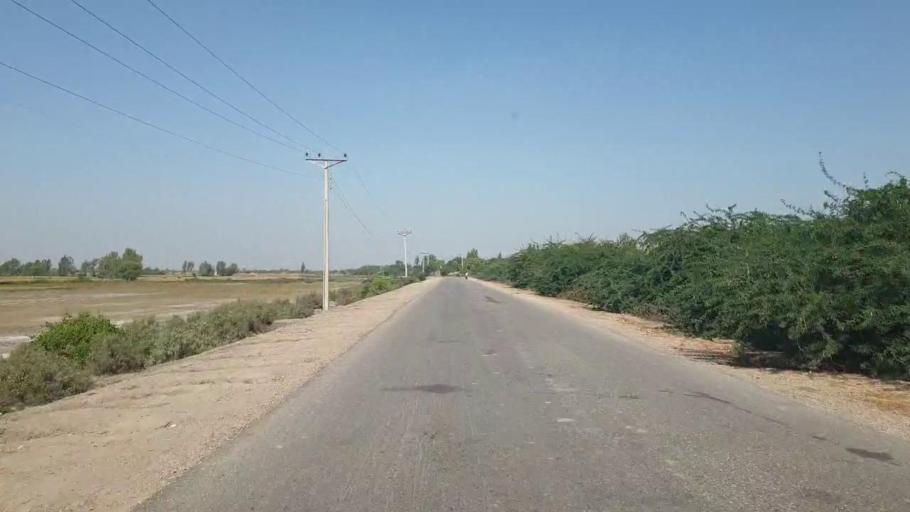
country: PK
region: Sindh
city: Talhar
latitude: 24.9191
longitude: 68.8607
